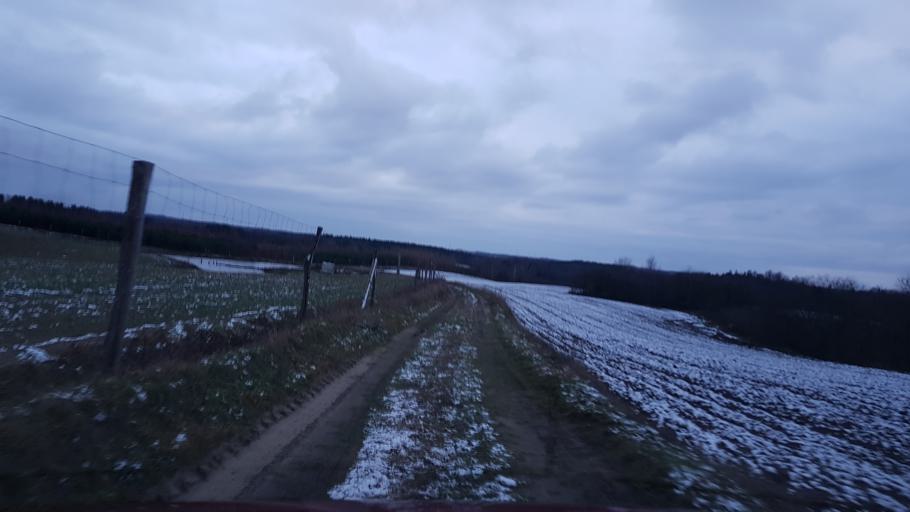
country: PL
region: Pomeranian Voivodeship
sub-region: Powiat bytowski
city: Tuchomie
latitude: 54.1492
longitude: 17.3037
